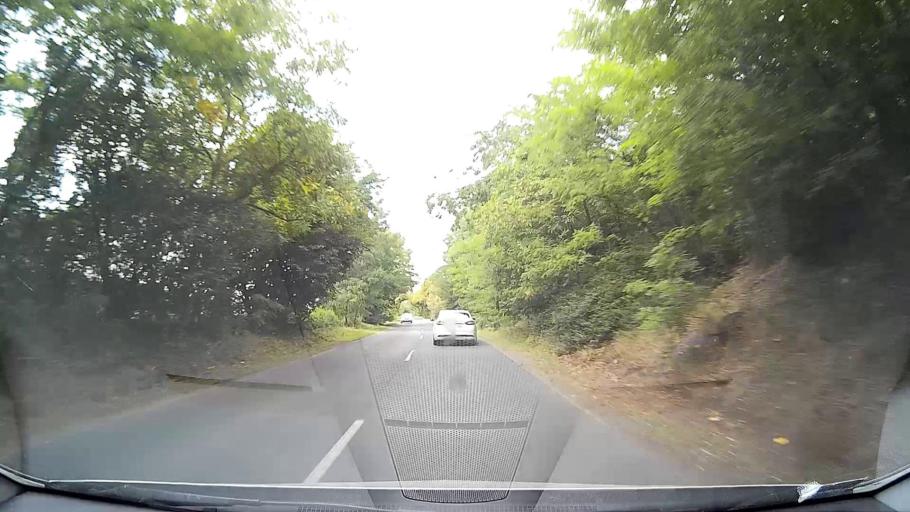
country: HU
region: Pest
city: Tahitotfalu
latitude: 47.7351
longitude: 19.1029
